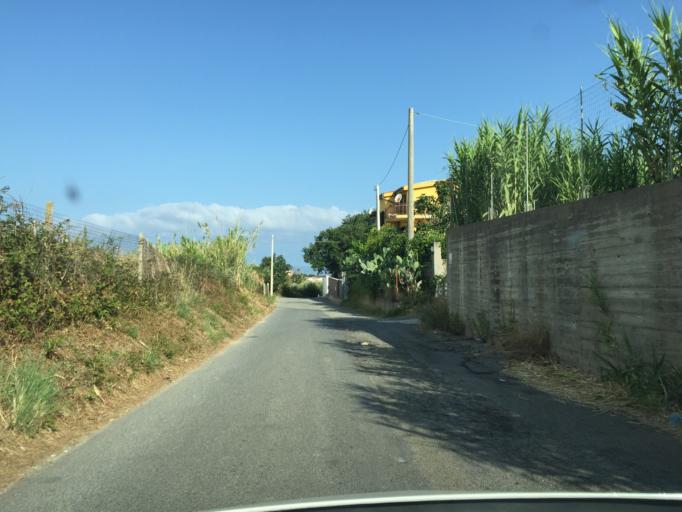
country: IT
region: Calabria
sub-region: Provincia di Vibo-Valentia
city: Pannaconi
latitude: 38.7169
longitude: 16.0595
